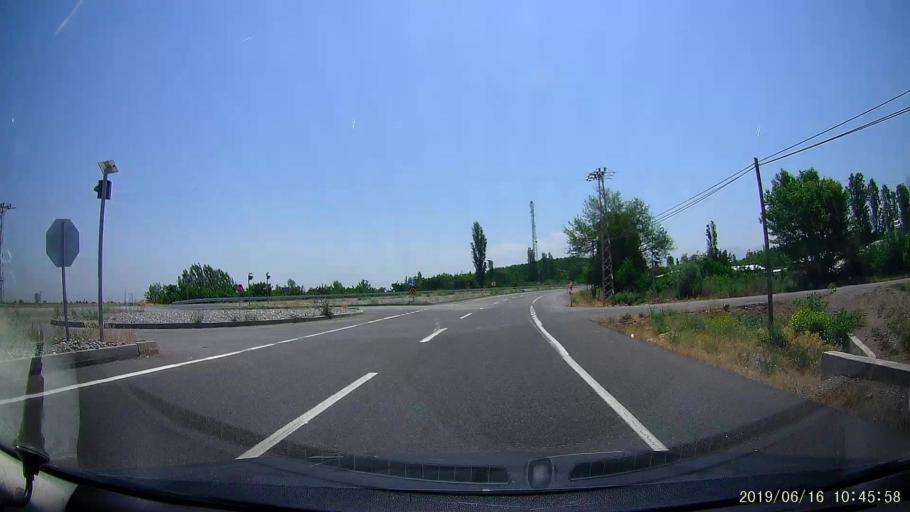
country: AM
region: Armavir
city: Shenavan
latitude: 40.0256
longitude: 43.8756
